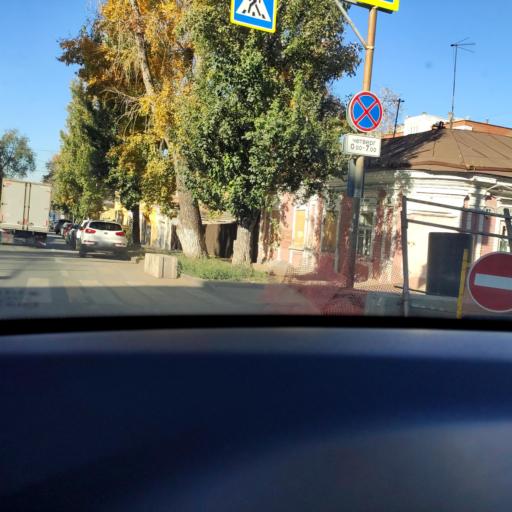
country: RU
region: Samara
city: Rozhdestveno
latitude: 53.1867
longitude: 50.0834
